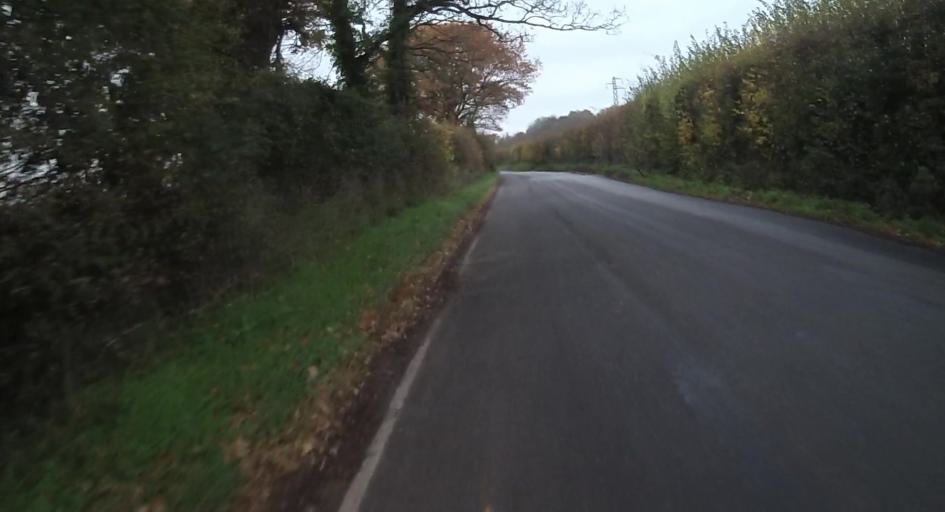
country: GB
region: England
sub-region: Wokingham
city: Swallowfield
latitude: 51.3798
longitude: -0.9348
